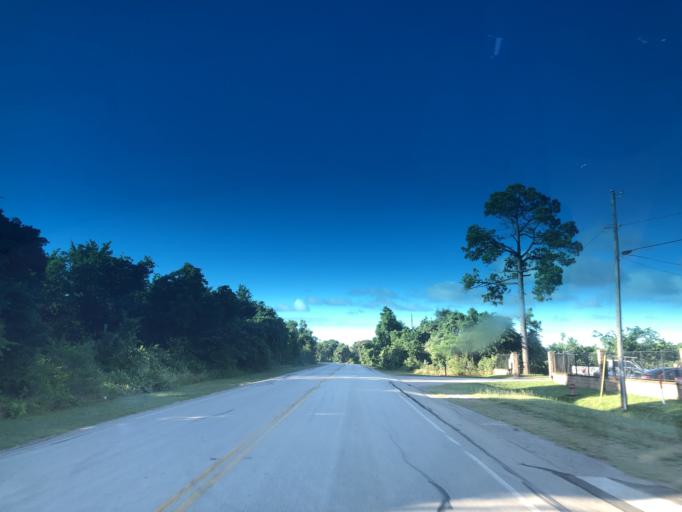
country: US
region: Texas
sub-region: Dallas County
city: Grand Prairie
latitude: 32.7838
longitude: -97.0169
